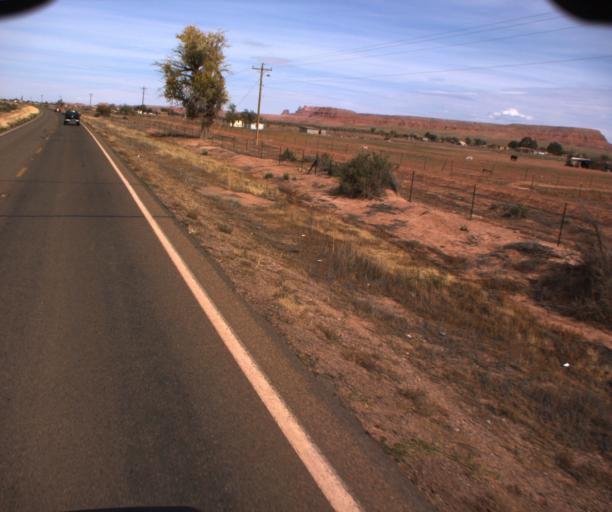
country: US
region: Arizona
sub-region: Apache County
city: Many Farms
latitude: 36.4189
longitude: -109.6065
